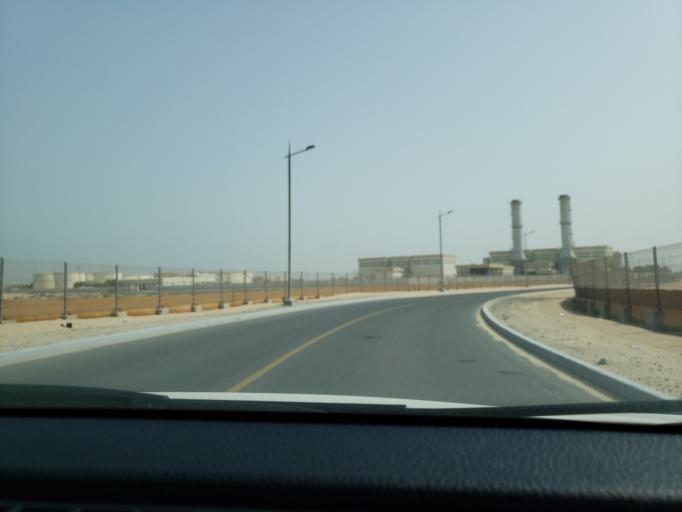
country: AE
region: Ajman
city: Ajman
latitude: 25.4411
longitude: 55.4762
